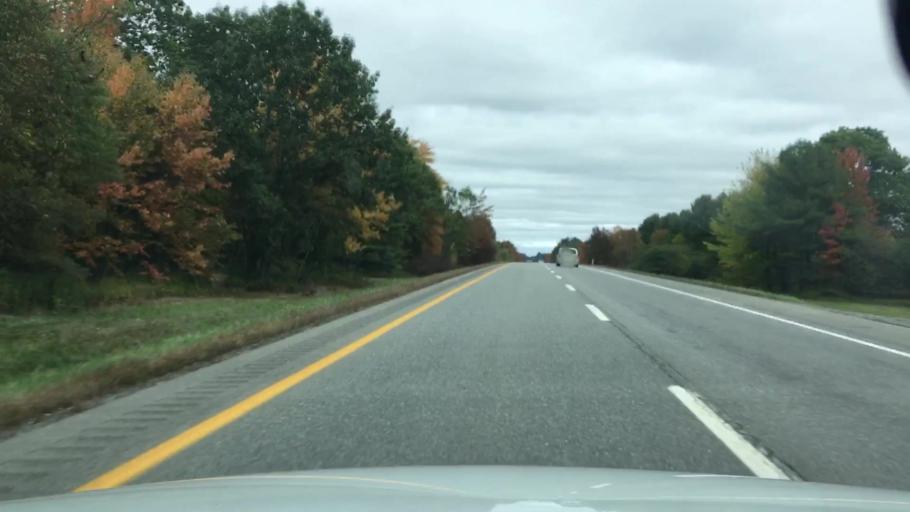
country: US
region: Maine
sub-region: Somerset County
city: Fairfield
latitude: 44.6056
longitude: -69.5757
